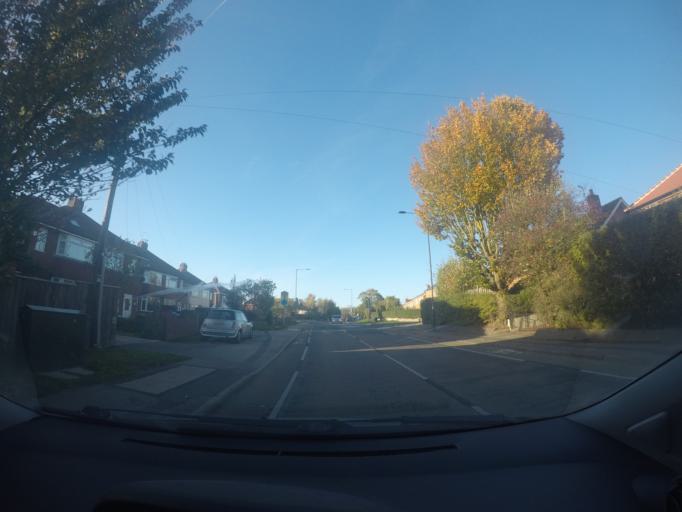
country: GB
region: England
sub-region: City of York
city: Huntington
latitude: 53.9824
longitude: -1.0679
